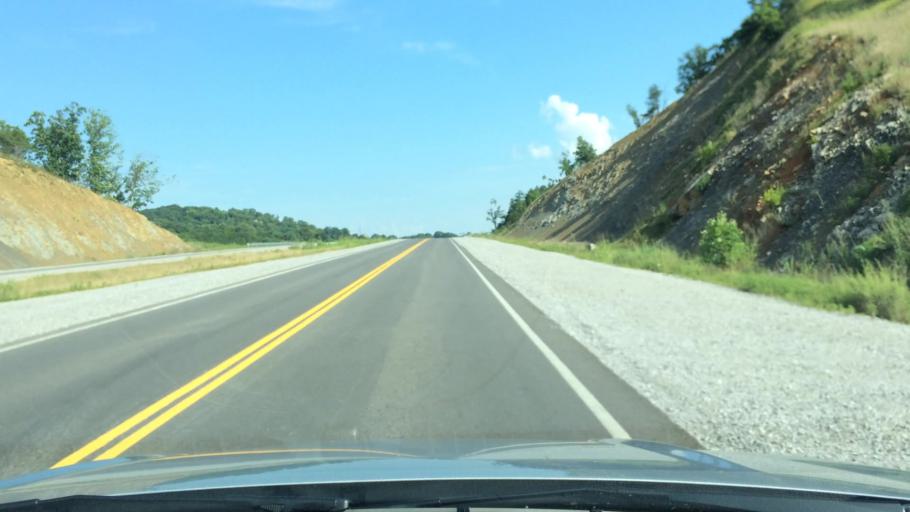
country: US
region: Tennessee
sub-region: Jefferson County
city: White Pine
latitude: 36.1355
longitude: -83.3379
